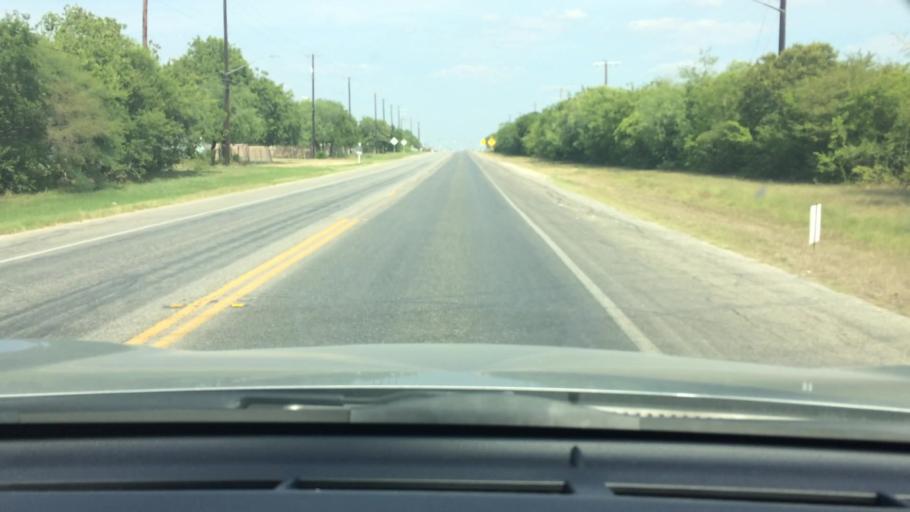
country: US
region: Texas
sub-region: Bexar County
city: China Grove
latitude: 29.3264
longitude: -98.4326
